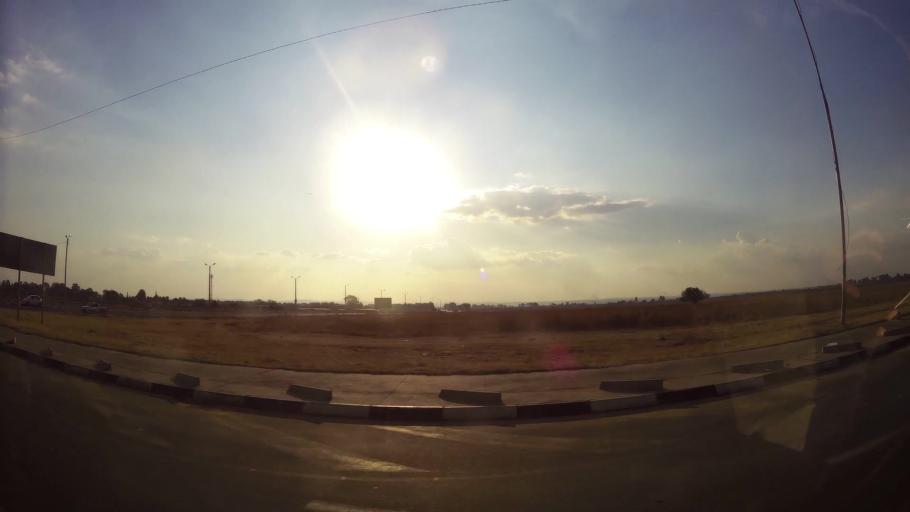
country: ZA
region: Gauteng
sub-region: Ekurhuleni Metropolitan Municipality
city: Germiston
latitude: -26.3337
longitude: 28.2324
